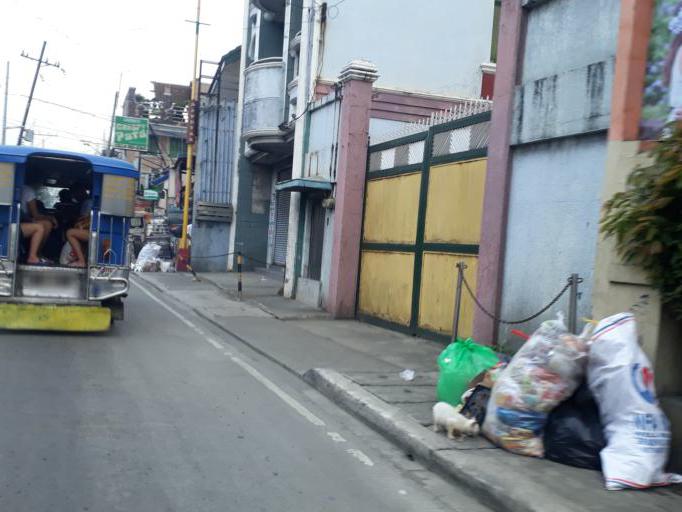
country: PH
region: Calabarzon
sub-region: Province of Rizal
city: Navotas
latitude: 14.6612
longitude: 120.9461
